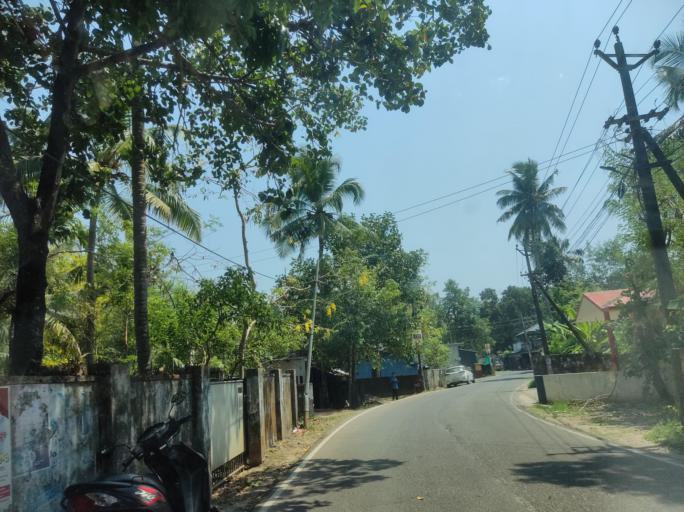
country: IN
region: Kerala
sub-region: Alappuzha
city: Kutiatodu
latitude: 9.8381
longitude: 76.2964
